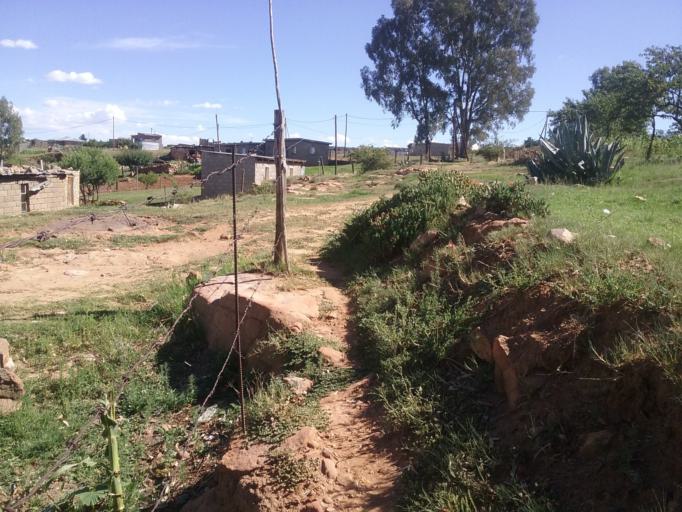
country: LS
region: Maseru
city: Maseru
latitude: -29.4166
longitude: 27.5675
